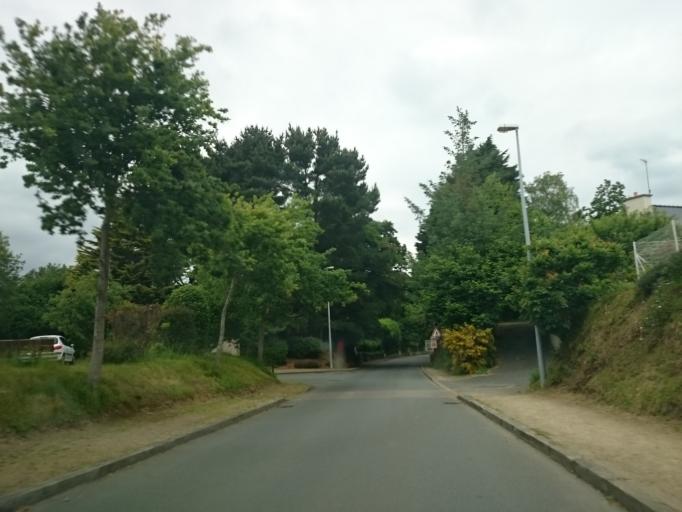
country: FR
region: Brittany
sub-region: Departement des Cotes-d'Armor
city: Louannec
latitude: 48.7910
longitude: -3.4122
